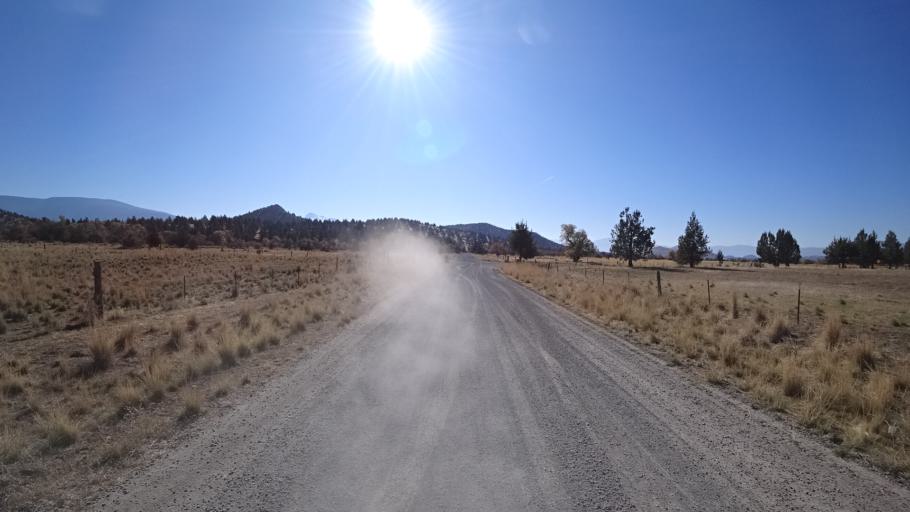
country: US
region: California
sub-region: Siskiyou County
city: Montague
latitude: 41.7270
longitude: -122.3695
